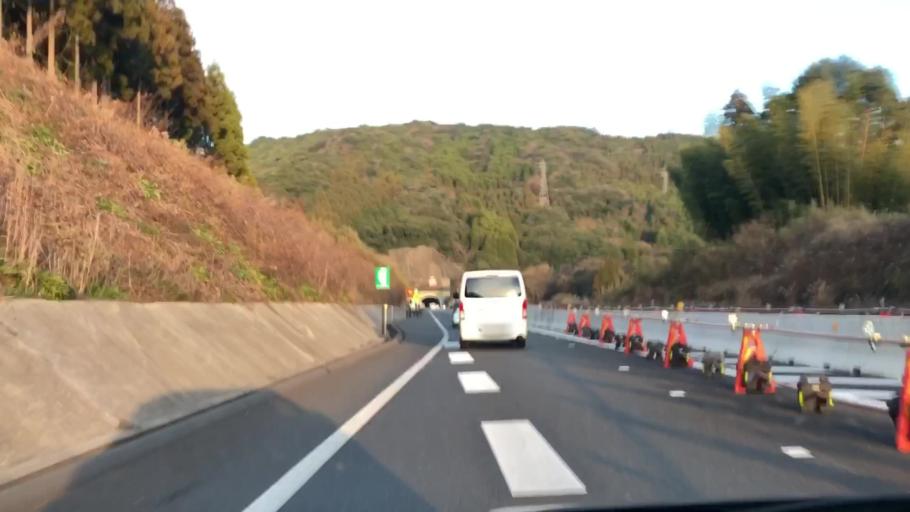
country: JP
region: Kumamoto
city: Minamata
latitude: 32.2436
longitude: 130.4736
